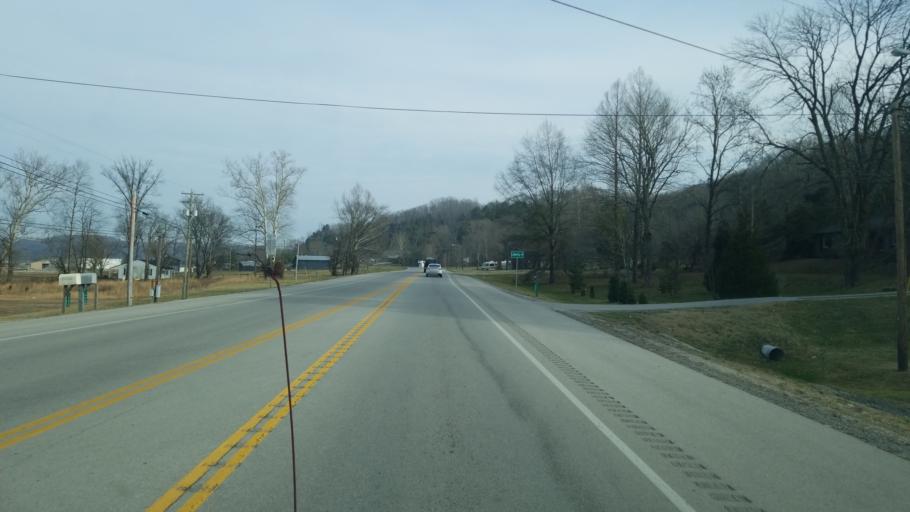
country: US
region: Kentucky
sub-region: Casey County
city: Liberty
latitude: 37.2989
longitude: -84.9491
